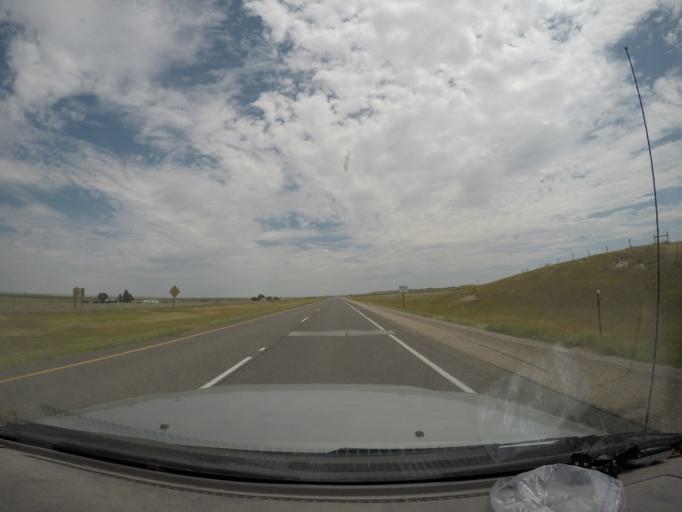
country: US
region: Wyoming
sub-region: Laramie County
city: Pine Bluffs
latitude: 41.1851
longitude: -104.0323
